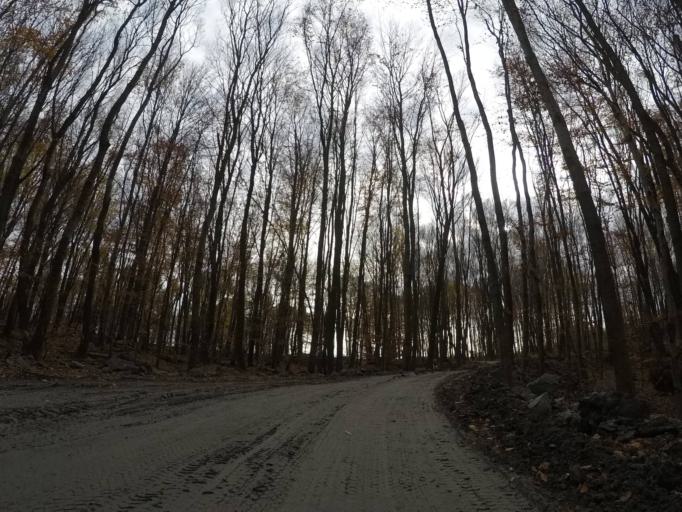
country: SK
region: Presovsky
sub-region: Okres Presov
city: Presov
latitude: 48.9727
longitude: 21.2171
